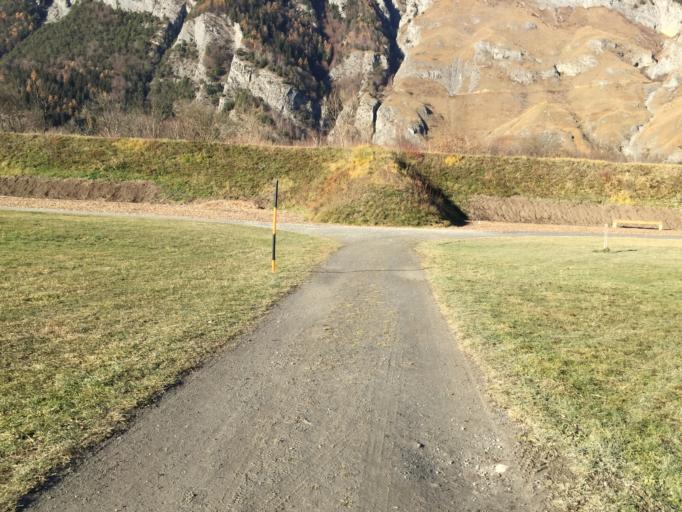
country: CH
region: Grisons
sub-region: Imboden District
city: Felsberg
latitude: 46.8514
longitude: 9.4960
